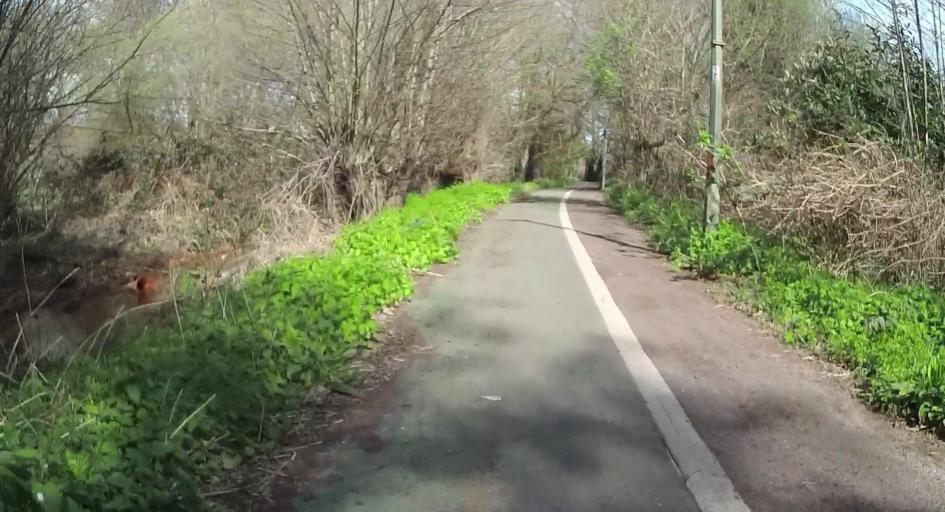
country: GB
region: England
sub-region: Surrey
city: Chertsey
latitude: 51.3812
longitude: -0.5031
